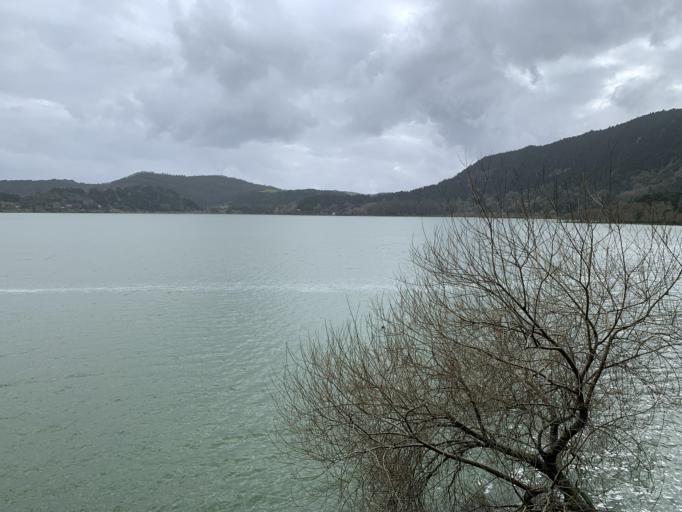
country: PT
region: Azores
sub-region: Povoacao
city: Furnas
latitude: 37.7615
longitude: -25.3404
